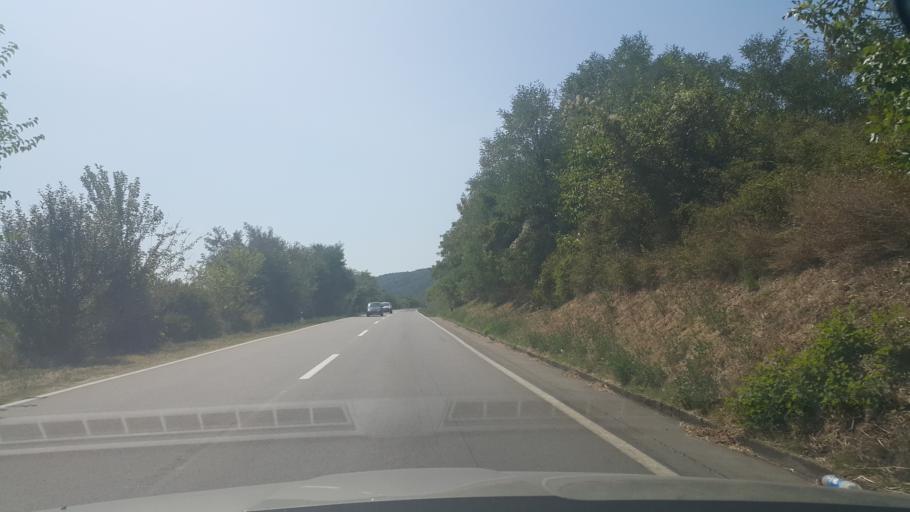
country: RS
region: Central Serbia
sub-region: Zajecarski Okrug
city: Zajecar
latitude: 43.8264
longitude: 22.2882
